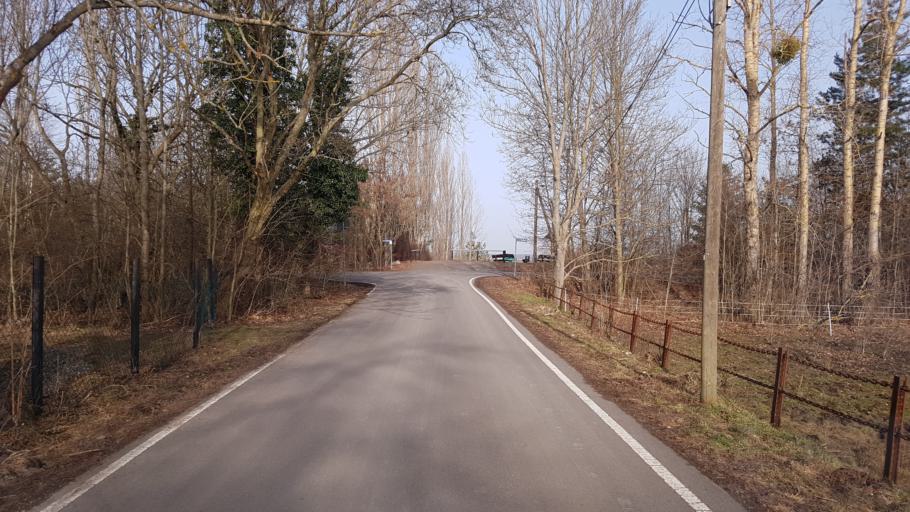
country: DE
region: Brandenburg
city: Schipkau
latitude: 51.5306
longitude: 13.8300
